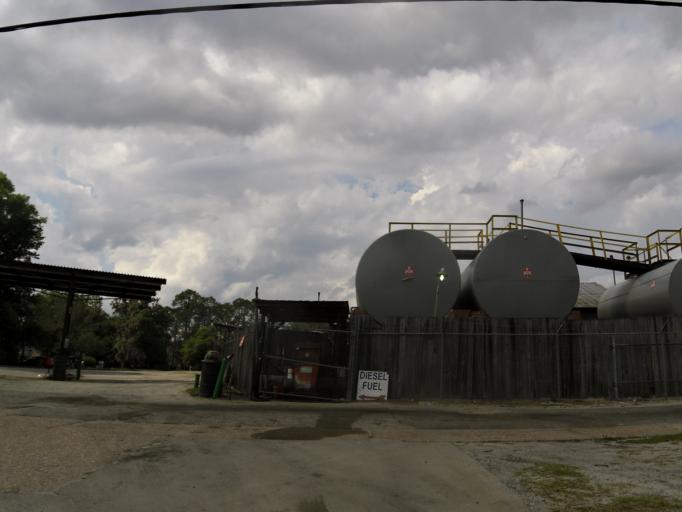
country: US
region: Georgia
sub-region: Charlton County
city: Folkston
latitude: 30.8307
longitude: -82.0105
